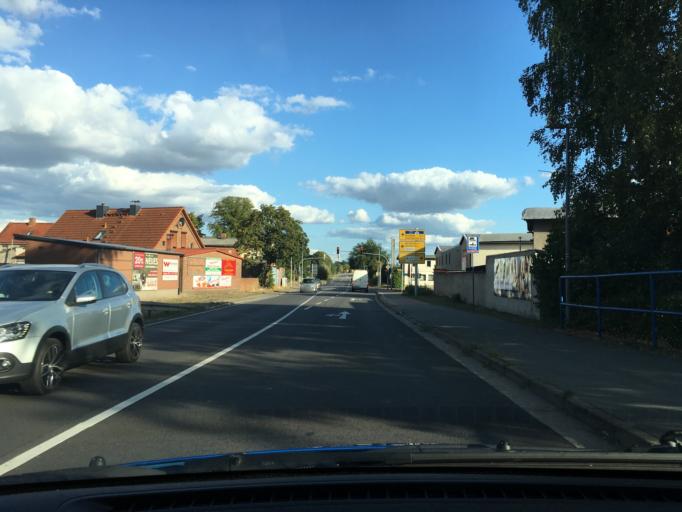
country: DE
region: Mecklenburg-Vorpommern
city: Grabow
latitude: 53.2753
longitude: 11.5588
